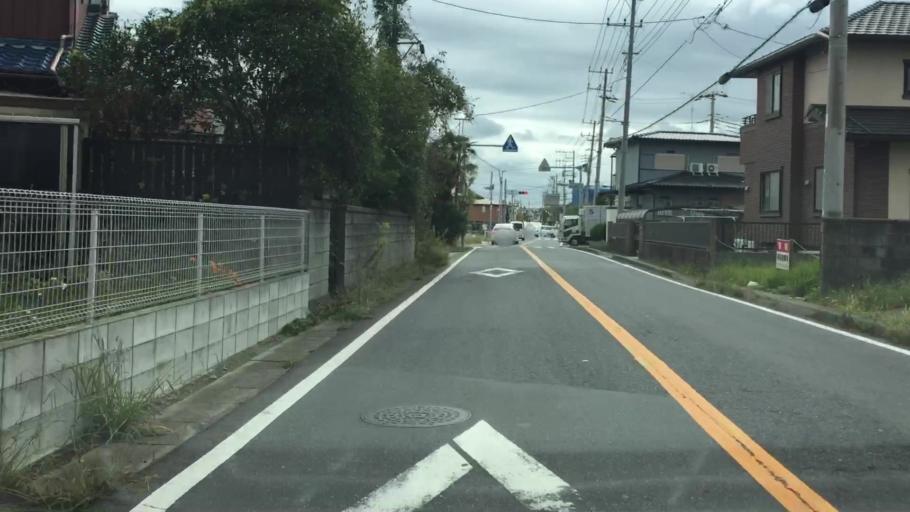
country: JP
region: Ibaraki
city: Ryugasaki
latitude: 35.8500
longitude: 140.1399
